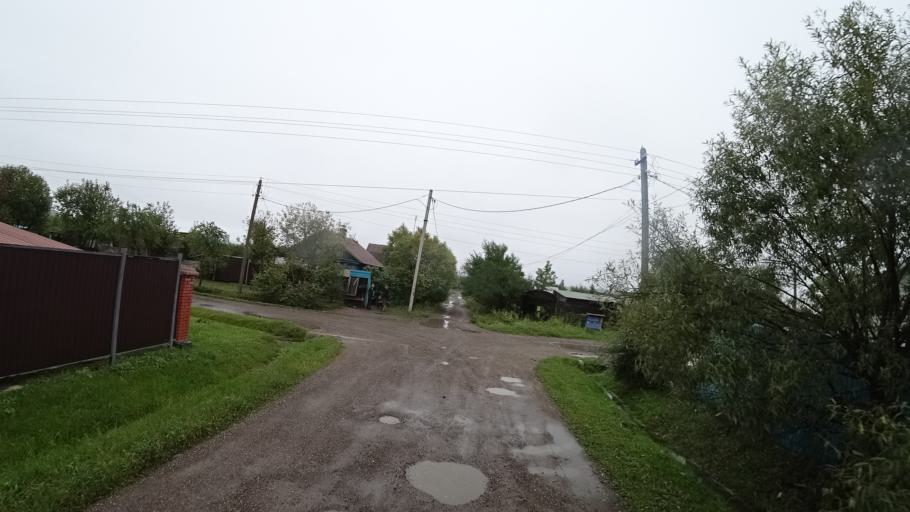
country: RU
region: Primorskiy
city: Monastyrishche
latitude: 44.2089
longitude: 132.4515
